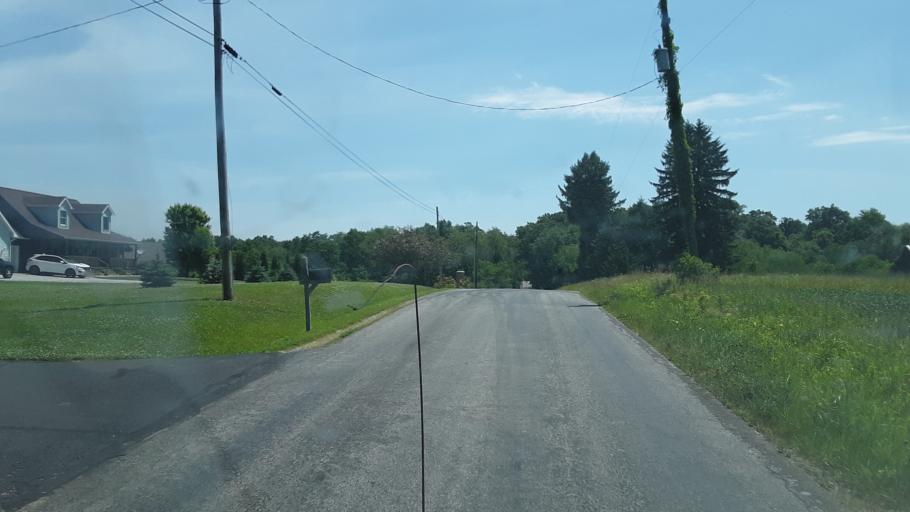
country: US
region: Ohio
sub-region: Wayne County
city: Shreve
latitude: 40.7196
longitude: -82.0366
